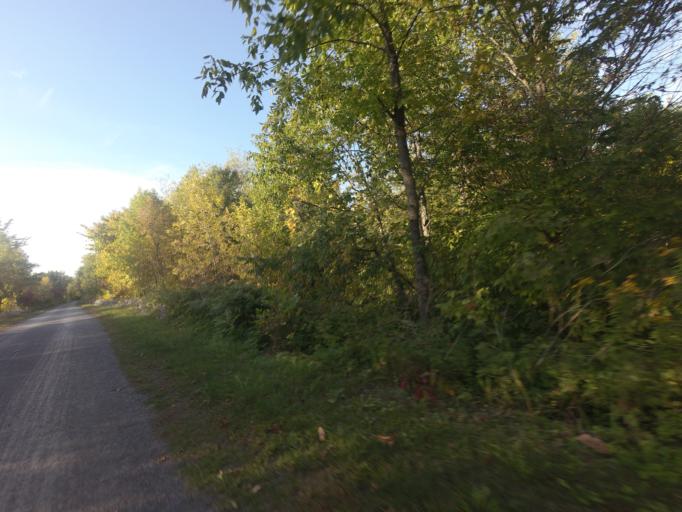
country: CA
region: Quebec
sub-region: Laurentides
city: Prevost
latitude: 45.8471
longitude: -74.0623
